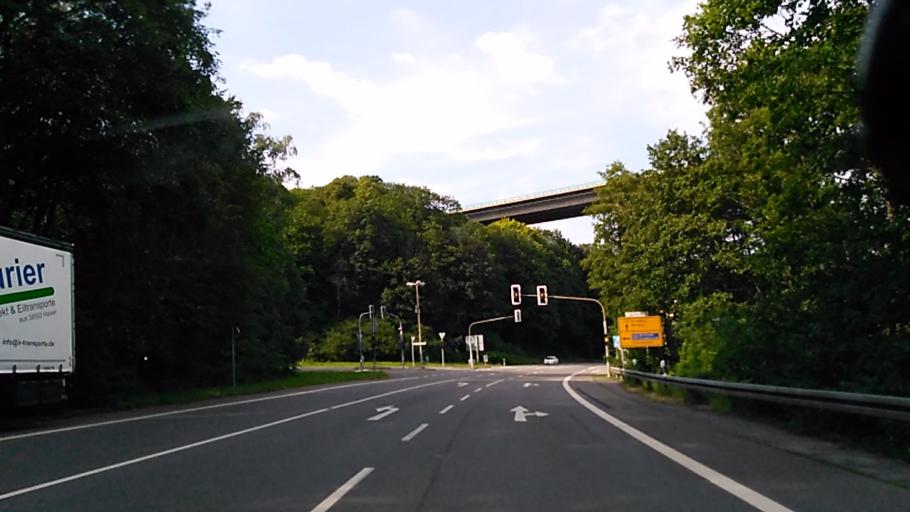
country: DE
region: North Rhine-Westphalia
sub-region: Regierungsbezirk Arnsberg
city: Luedenscheid
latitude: 51.2280
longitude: 7.6621
